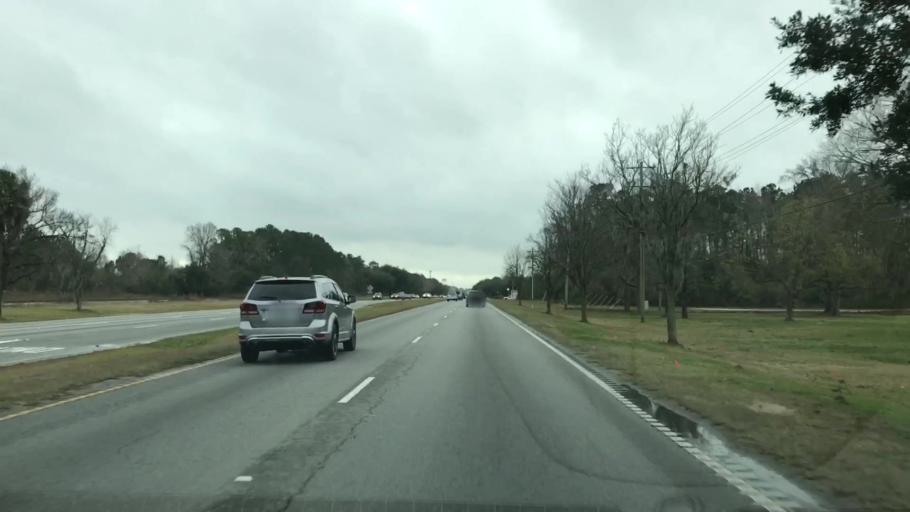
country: US
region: South Carolina
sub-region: Berkeley County
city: Goose Creek
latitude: 33.0326
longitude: -80.0345
